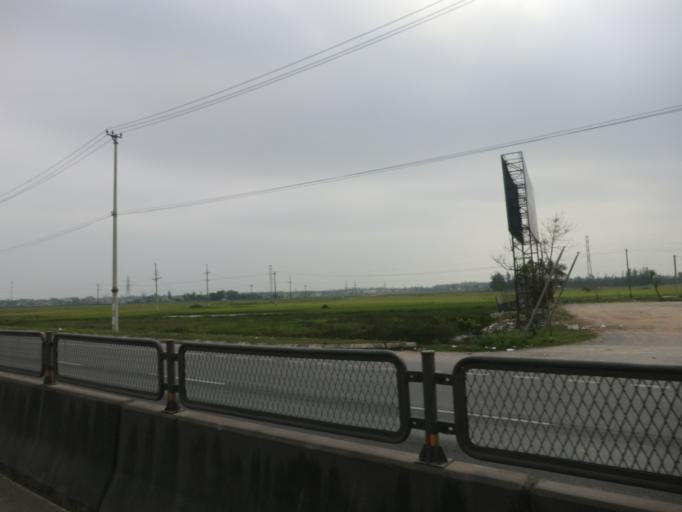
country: VN
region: Quang Binh
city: Ba Don
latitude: 17.7578
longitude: 106.4432
